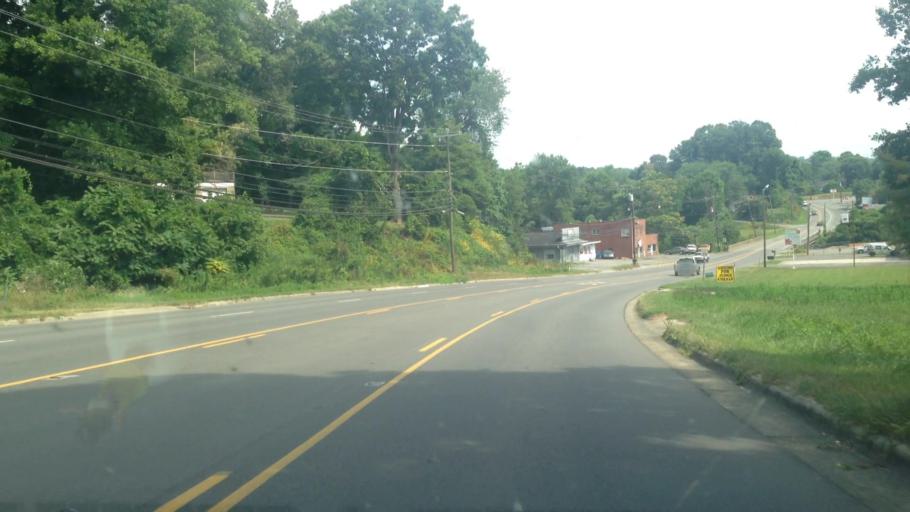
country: US
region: North Carolina
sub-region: Surry County
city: Mount Airy
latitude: 36.4932
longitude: -80.5967
